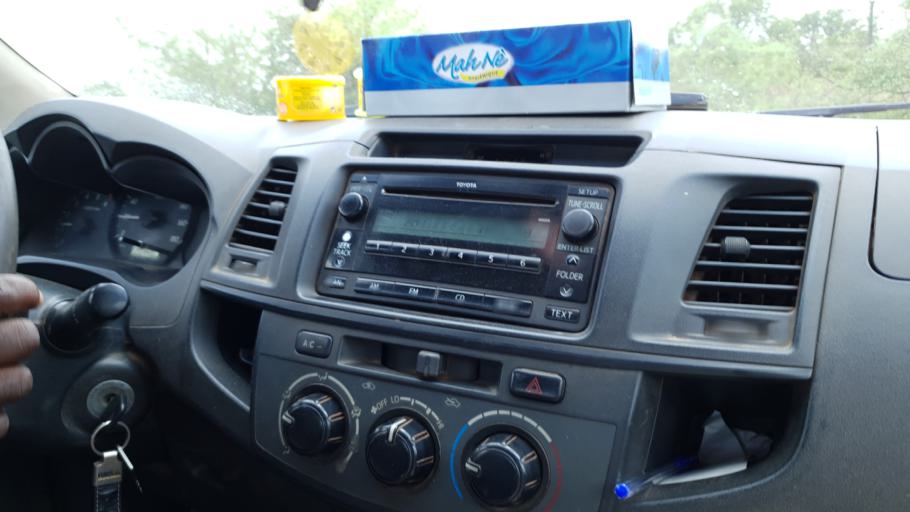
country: ML
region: Segou
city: Baroueli
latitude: 13.3477
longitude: -7.0944
